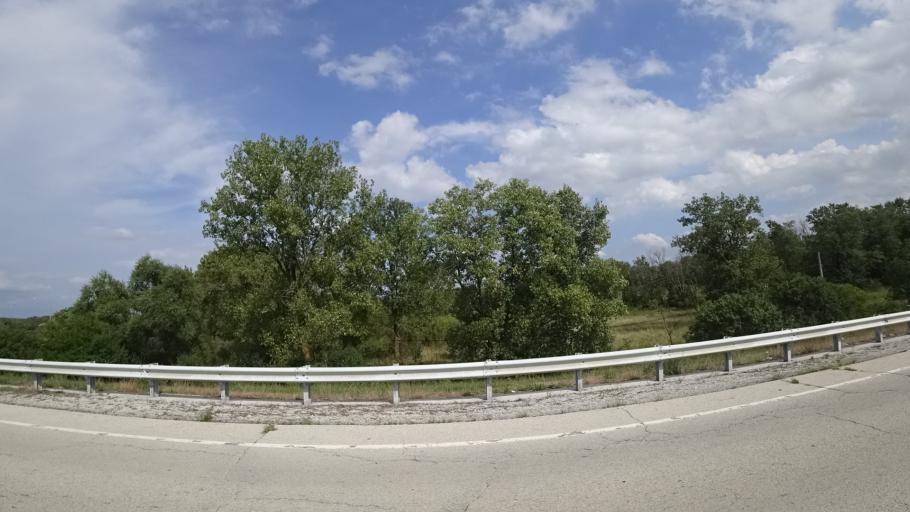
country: US
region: Illinois
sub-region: Cook County
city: Tinley Park
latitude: 41.5527
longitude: -87.7712
